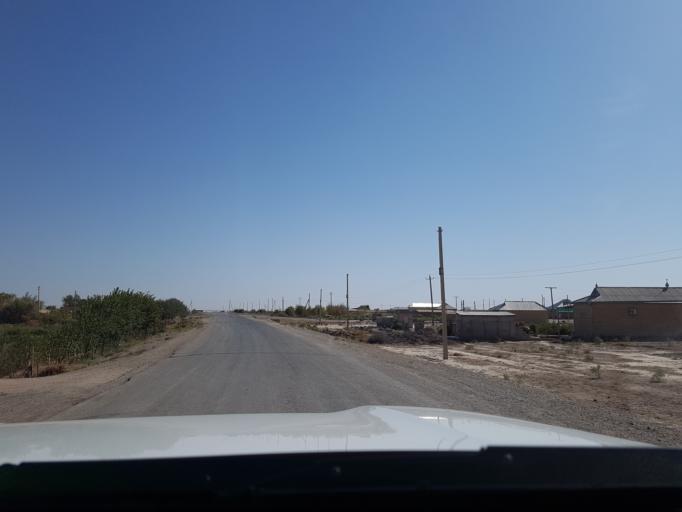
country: IR
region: Razavi Khorasan
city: Sarakhs
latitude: 36.5188
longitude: 61.2508
